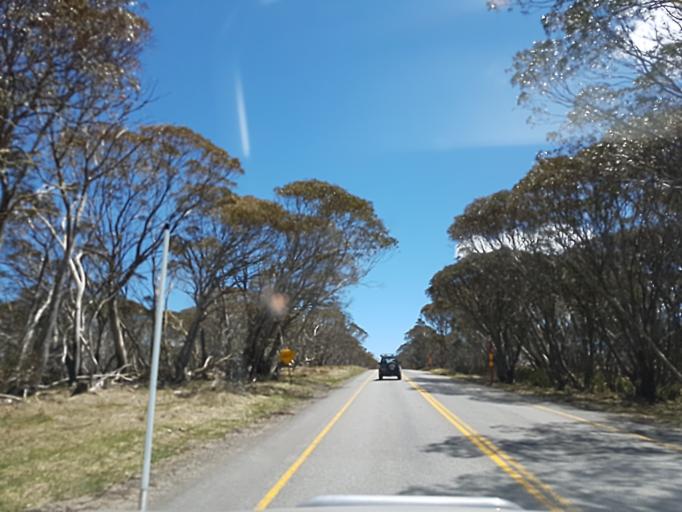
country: AU
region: Victoria
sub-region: Alpine
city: Mount Beauty
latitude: -37.0054
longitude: 147.1845
